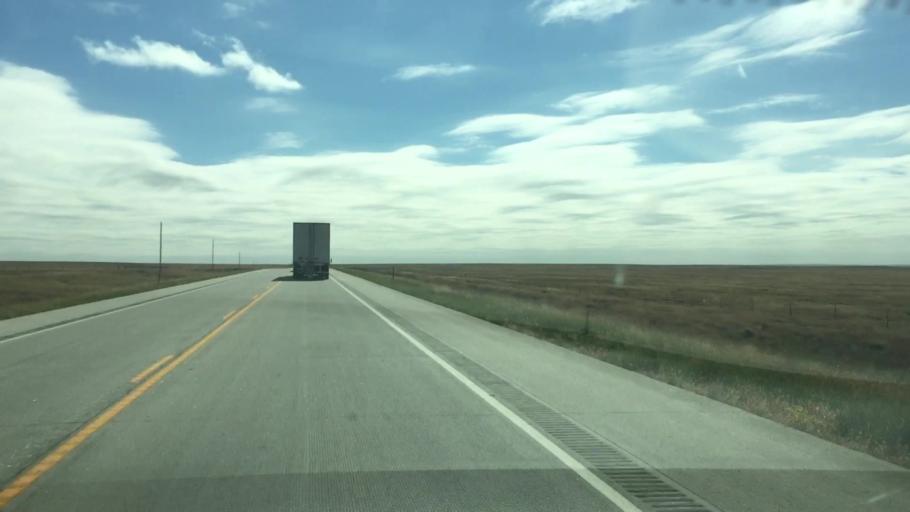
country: US
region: Colorado
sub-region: Lincoln County
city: Hugo
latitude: 39.0195
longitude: -103.3101
